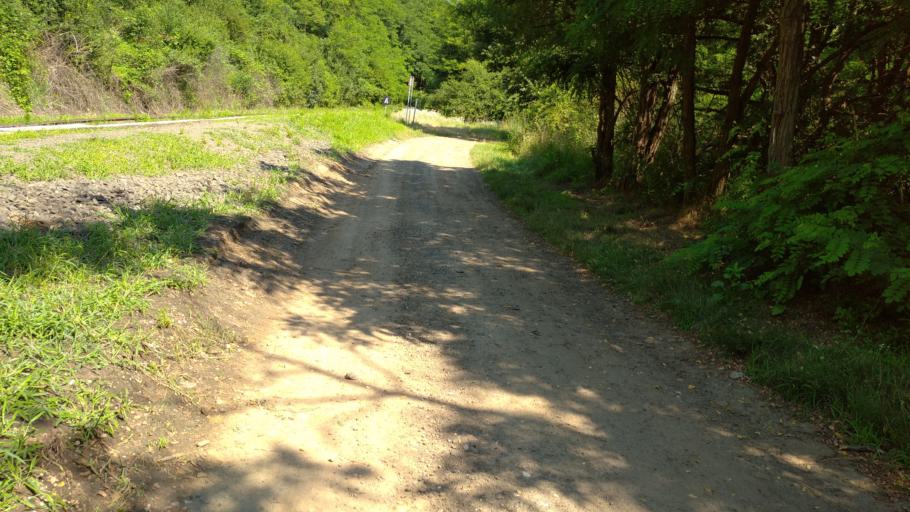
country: HU
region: Nograd
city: Nagyoroszi
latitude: 48.0285
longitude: 19.0445
